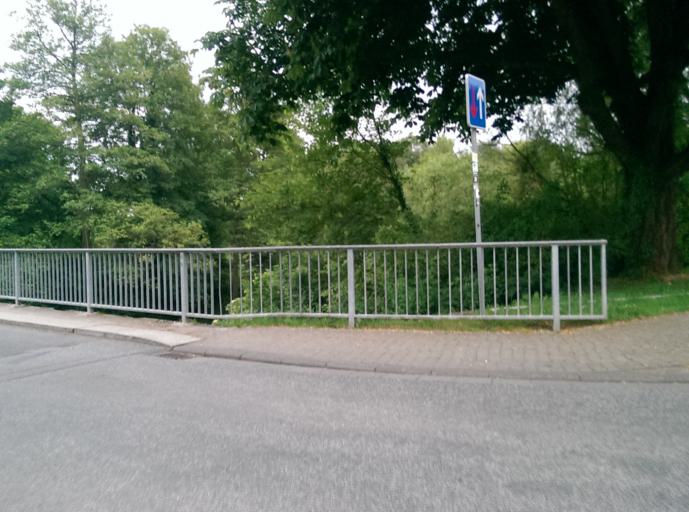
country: DE
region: Rheinland-Pfalz
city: Melsbach
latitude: 50.4694
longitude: 7.4661
